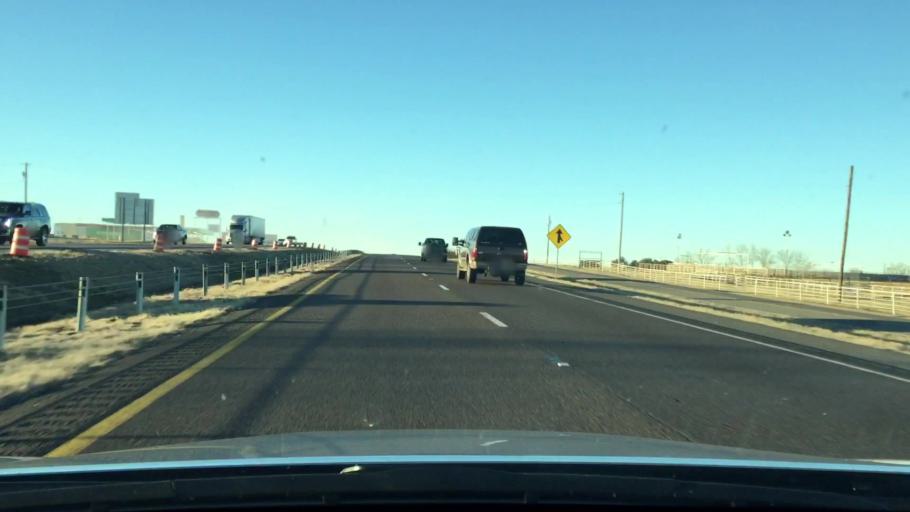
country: US
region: Texas
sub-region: Cooke County
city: Gainesville
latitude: 33.6829
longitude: -97.1569
